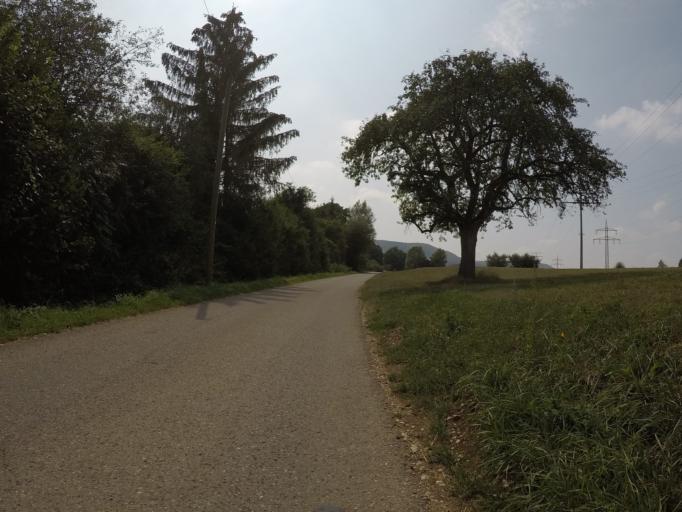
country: DE
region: Baden-Wuerttemberg
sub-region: Tuebingen Region
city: Pfullingen
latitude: 48.4491
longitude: 9.2064
